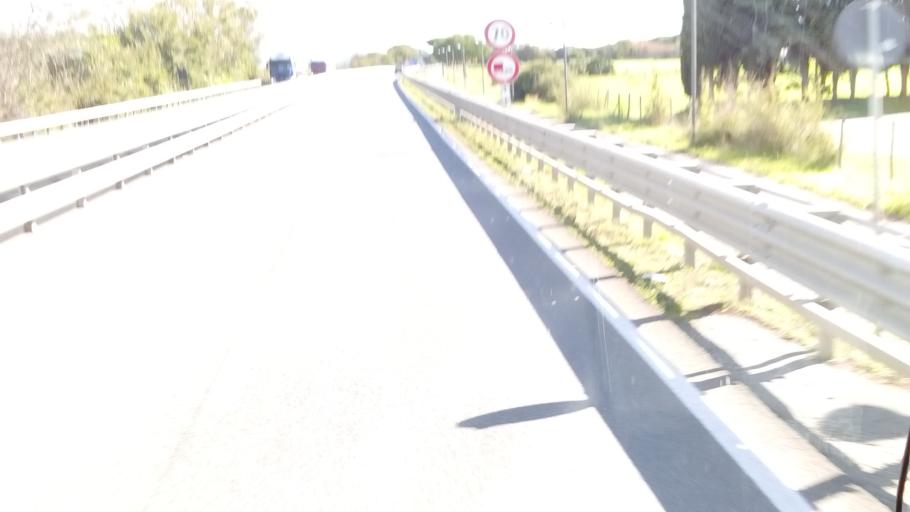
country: IT
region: Tuscany
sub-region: Provincia di Grosseto
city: Fonteblanda
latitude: 42.5453
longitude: 11.1773
